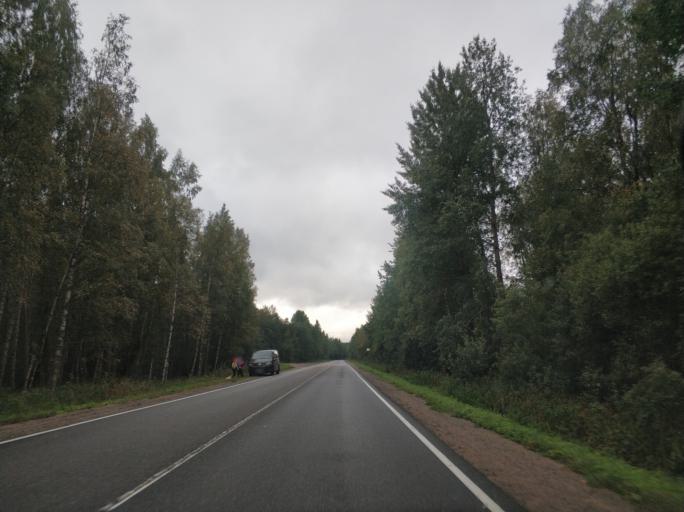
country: RU
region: Leningrad
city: Borisova Griva
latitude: 60.1196
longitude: 30.9636
